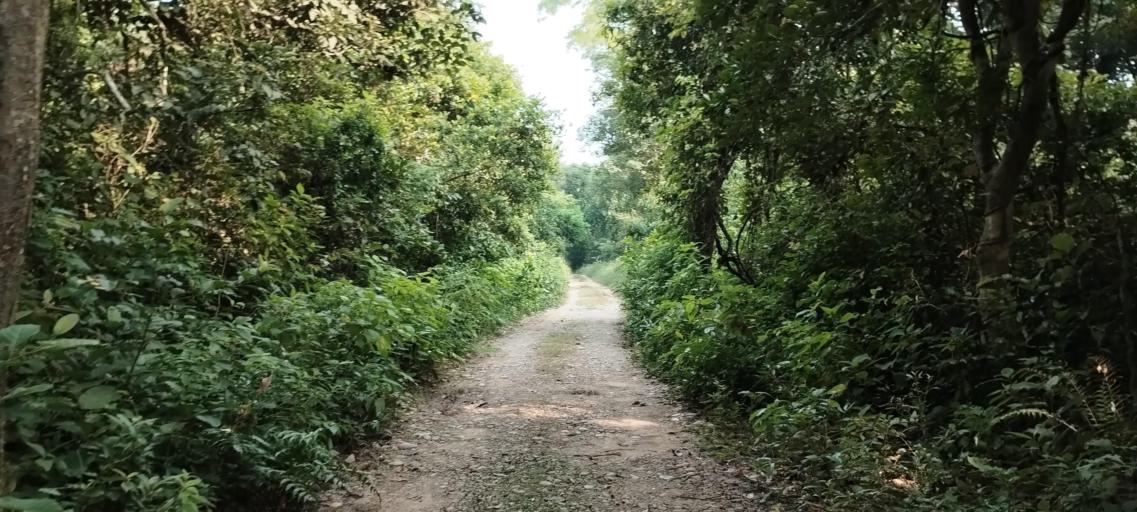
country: NP
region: Far Western
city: Tikapur
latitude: 28.4598
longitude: 81.2416
